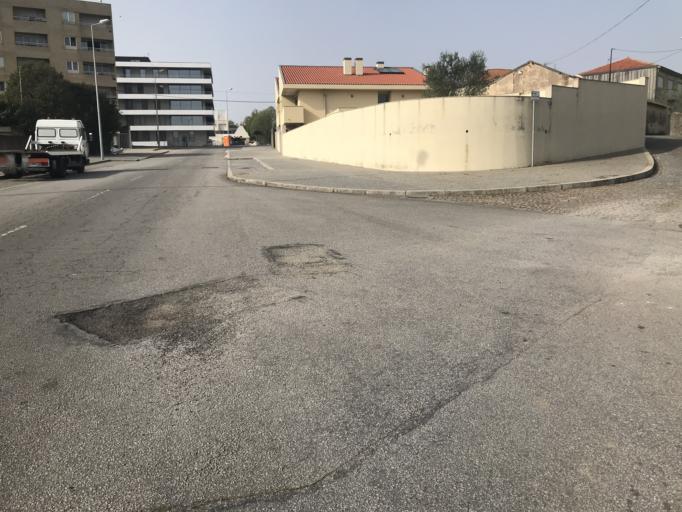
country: PT
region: Porto
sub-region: Matosinhos
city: Matosinhos
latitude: 41.1762
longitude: -8.6758
